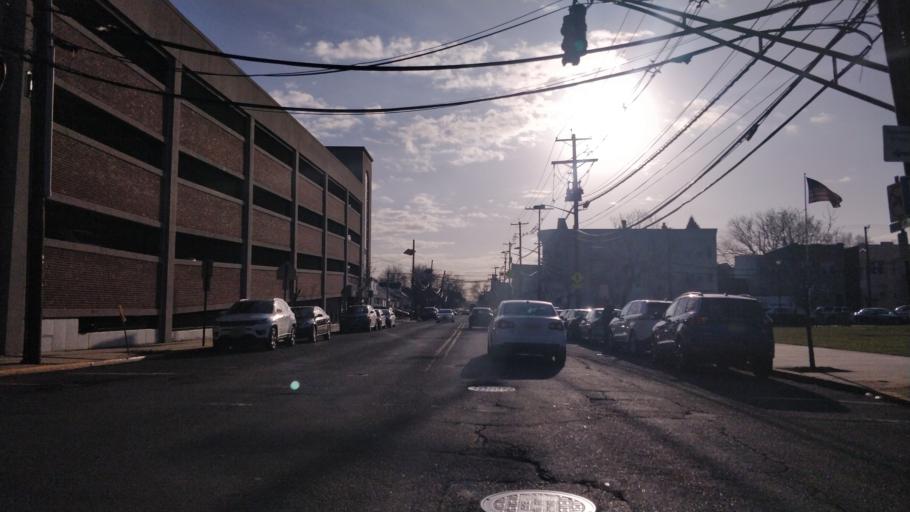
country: US
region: New Jersey
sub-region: Hudson County
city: Bayonne
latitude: 40.6680
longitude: -74.1116
